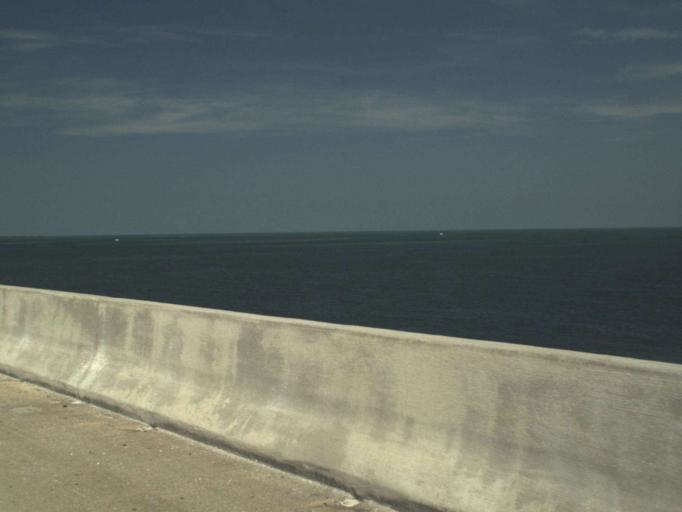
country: US
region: Florida
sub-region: Monroe County
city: Marathon
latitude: 24.7954
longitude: -80.8726
